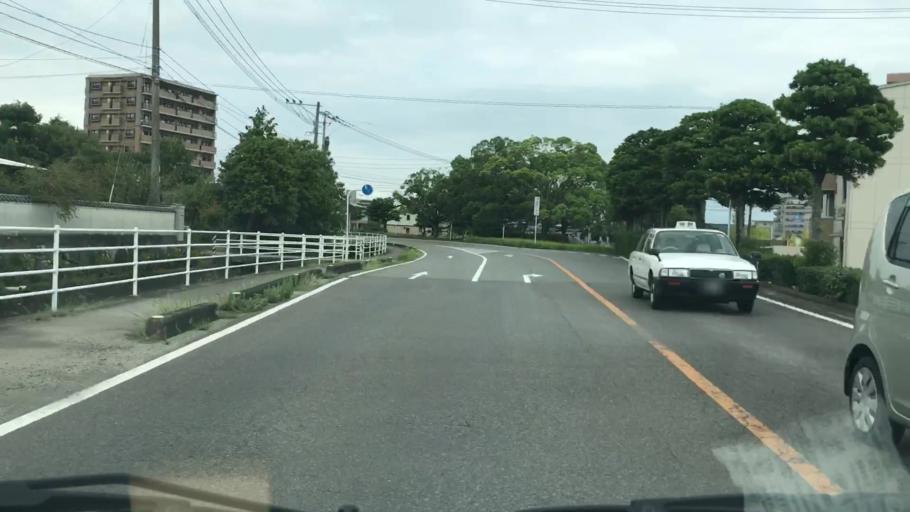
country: JP
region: Saga Prefecture
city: Saga-shi
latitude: 33.2768
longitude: 130.2625
